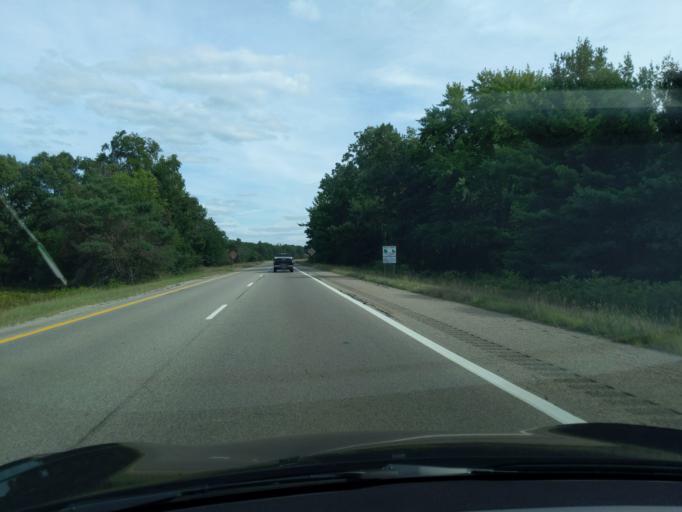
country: US
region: Michigan
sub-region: Muskegon County
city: Fruitport
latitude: 43.0948
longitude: -86.1019
